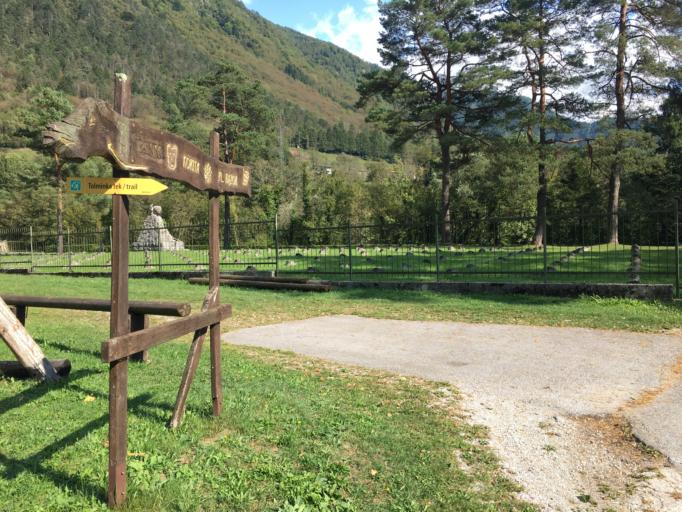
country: SI
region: Tolmin
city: Tolmin
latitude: 46.1917
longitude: 13.7355
